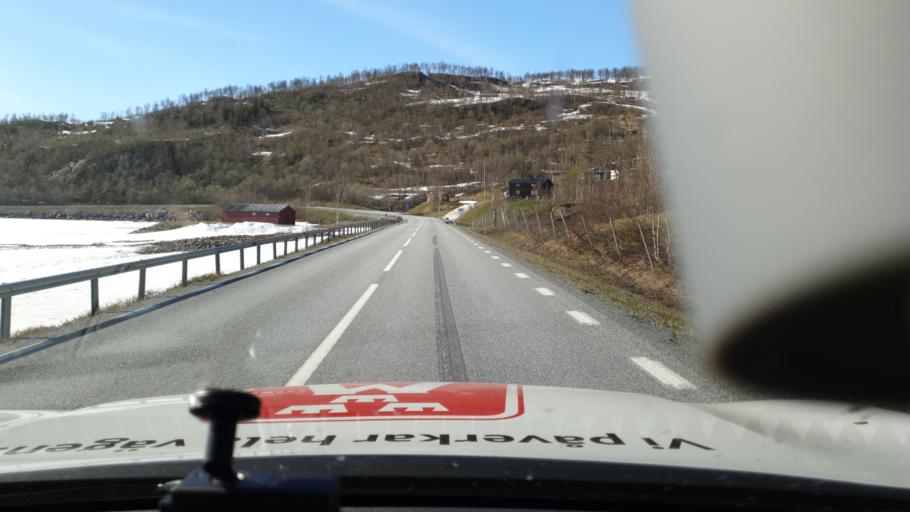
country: NO
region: Nordland
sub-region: Rana
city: Mo i Rana
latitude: 66.0999
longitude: 14.8487
